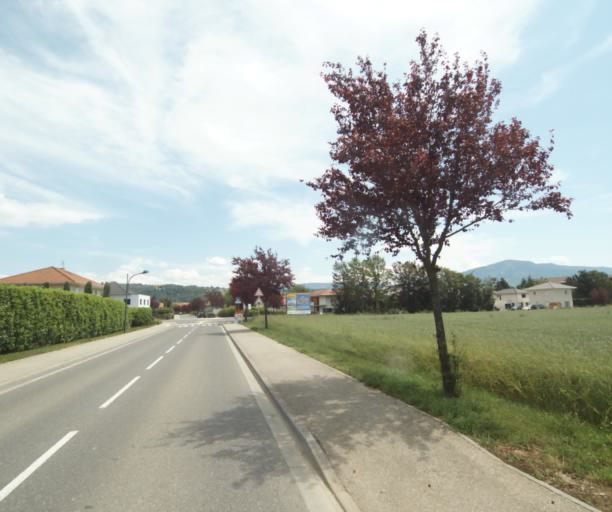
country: FR
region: Rhone-Alpes
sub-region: Departement de la Haute-Savoie
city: Douvaine
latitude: 46.3073
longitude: 6.2929
